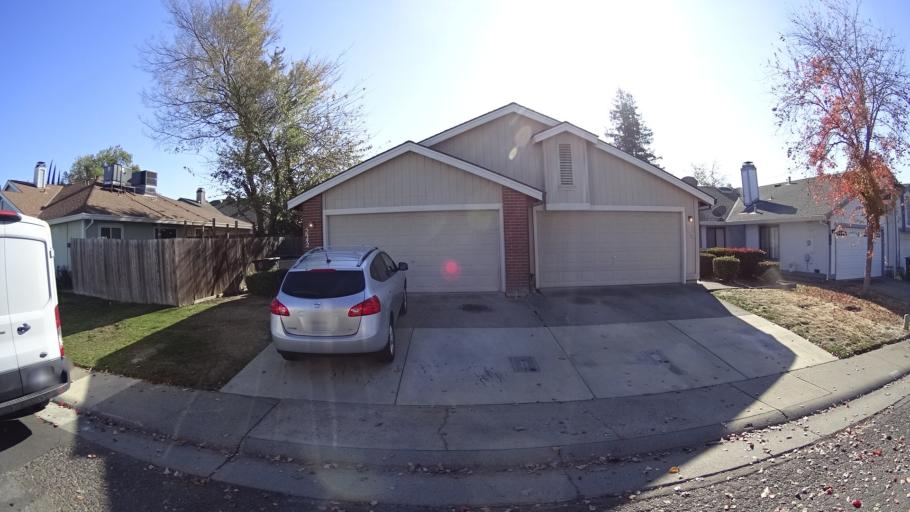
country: US
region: California
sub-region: Sacramento County
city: Citrus Heights
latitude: 38.6739
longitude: -121.2970
